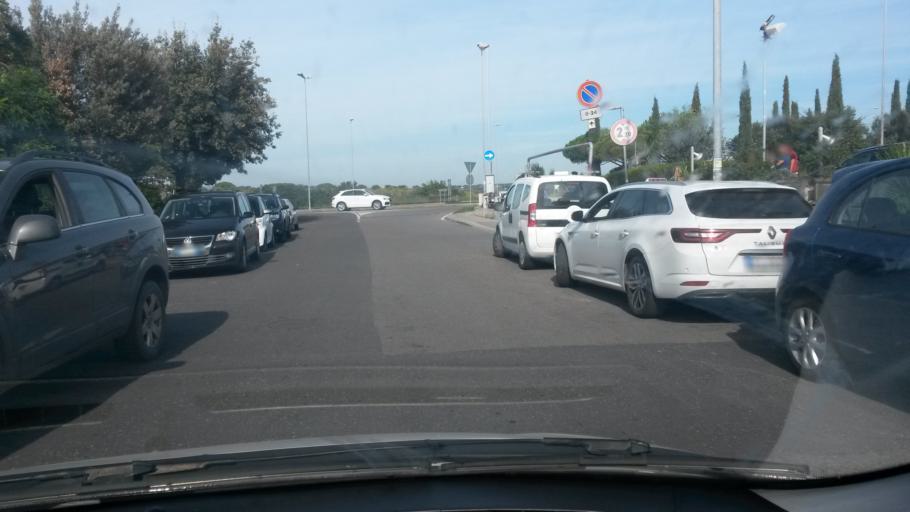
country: IT
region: Tuscany
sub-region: Provincia di Livorno
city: Cecina
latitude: 43.3135
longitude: 10.5335
